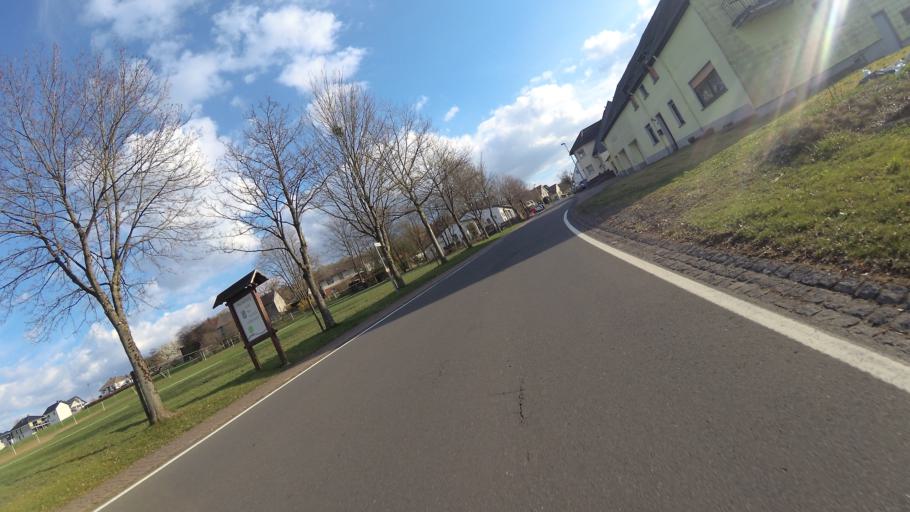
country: DE
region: Rheinland-Pfalz
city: Steiningen
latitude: 50.1820
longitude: 6.9150
